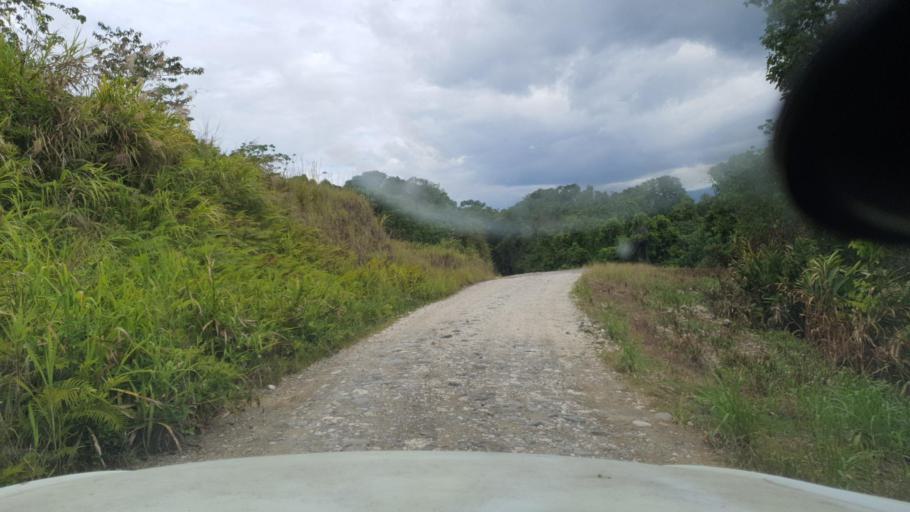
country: SB
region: Guadalcanal
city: Honiara
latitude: -9.4898
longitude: 160.0189
